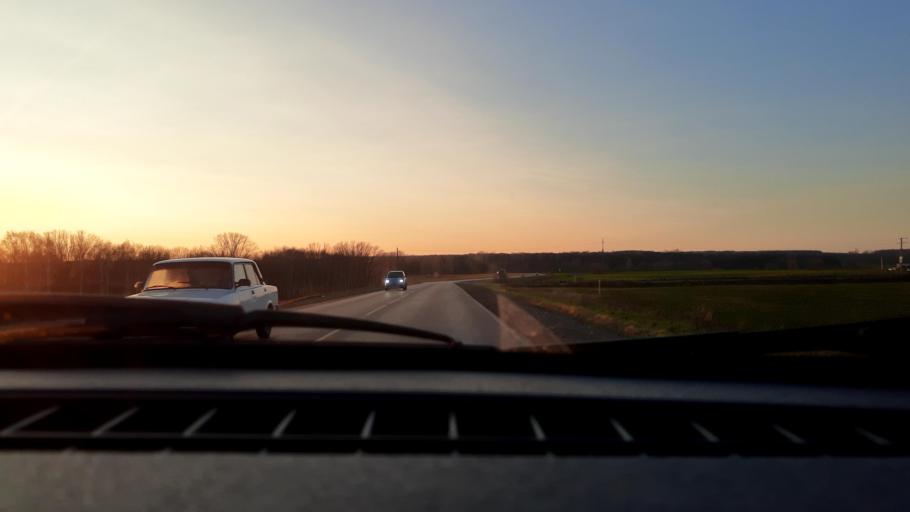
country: RU
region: Bashkortostan
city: Mikhaylovka
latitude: 54.8318
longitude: 55.9476
